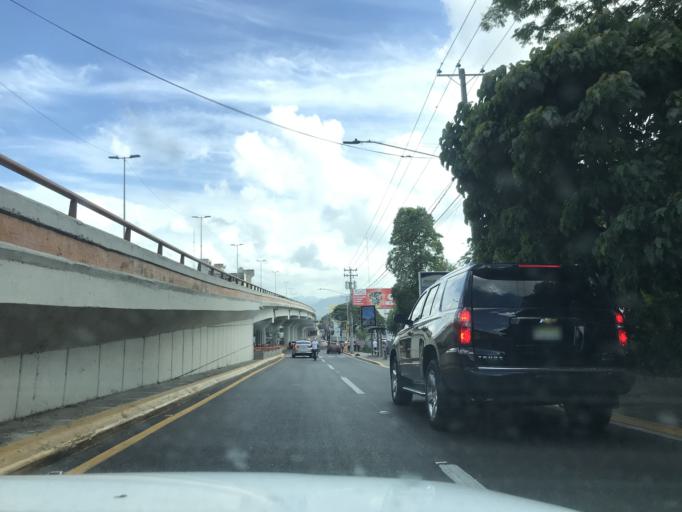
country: DO
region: Santiago
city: Santiago de los Caballeros
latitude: 19.4572
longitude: -70.6855
